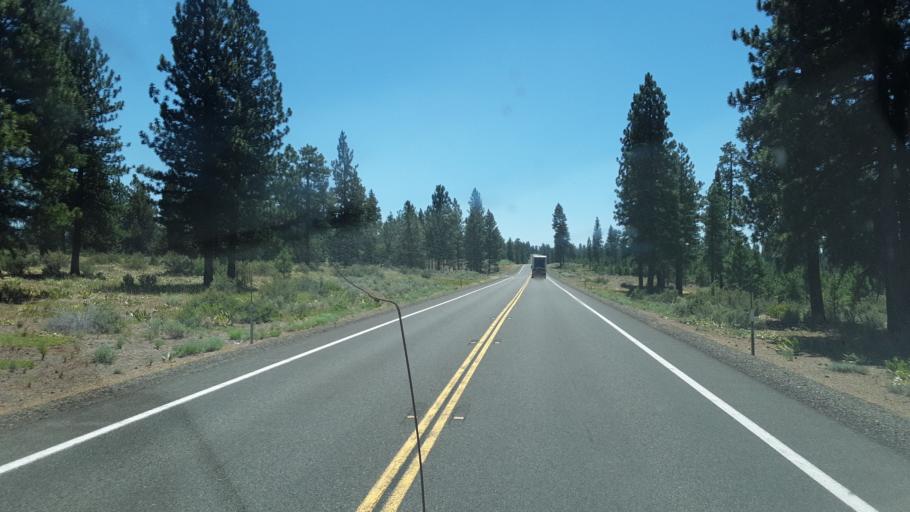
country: US
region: California
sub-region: Siskiyou County
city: Tulelake
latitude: 41.5945
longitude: -121.2000
